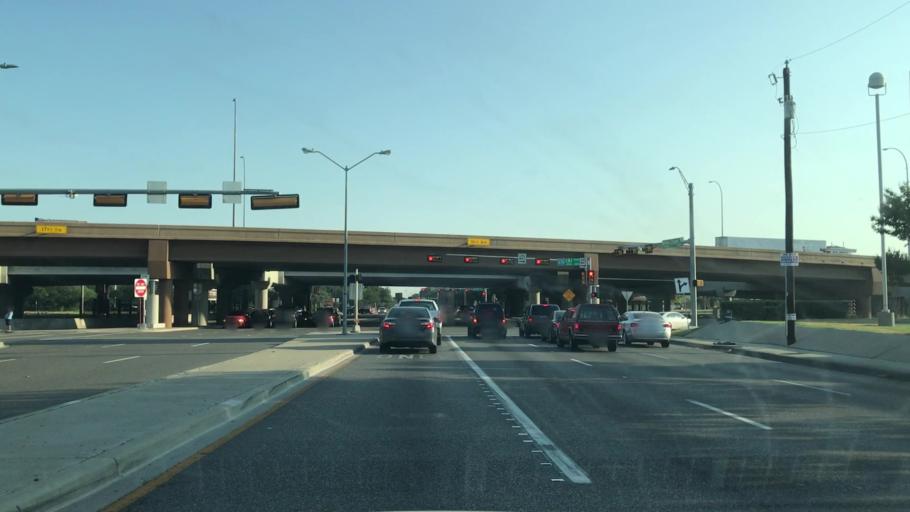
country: US
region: Texas
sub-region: Dallas County
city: Farmers Branch
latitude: 32.9119
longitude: -96.8733
